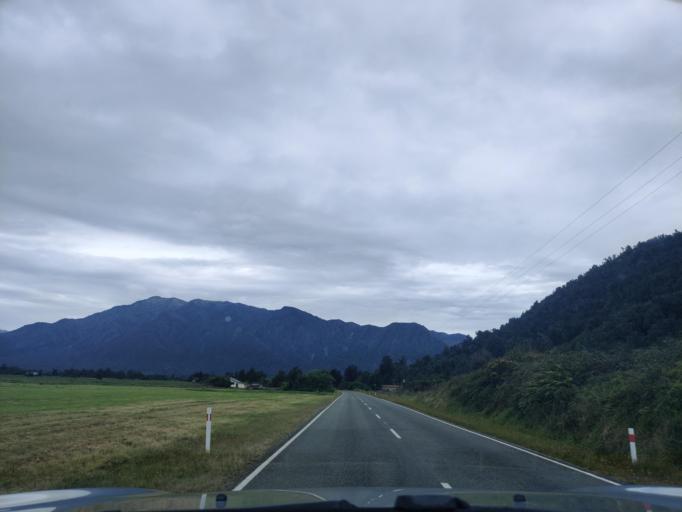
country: NZ
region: West Coast
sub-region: Westland District
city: Hokitika
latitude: -43.1531
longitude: 170.5807
